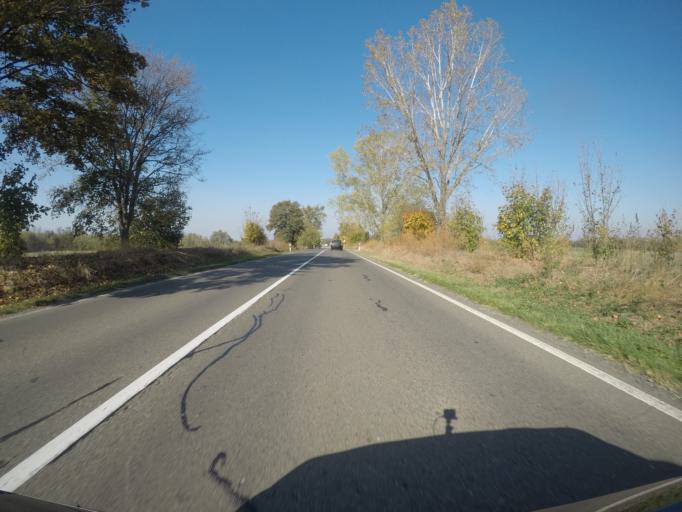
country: HU
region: Tolna
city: Tengelic
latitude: 46.5309
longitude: 18.6567
